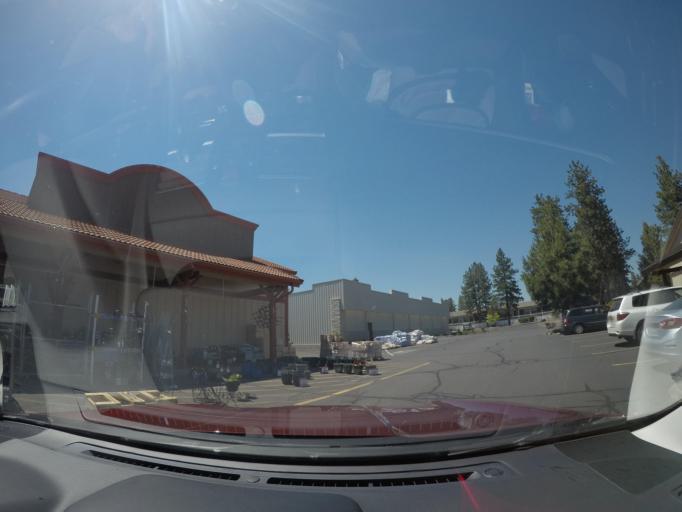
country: US
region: Oregon
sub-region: Deschutes County
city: Sisters
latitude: 44.2942
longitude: -121.5600
